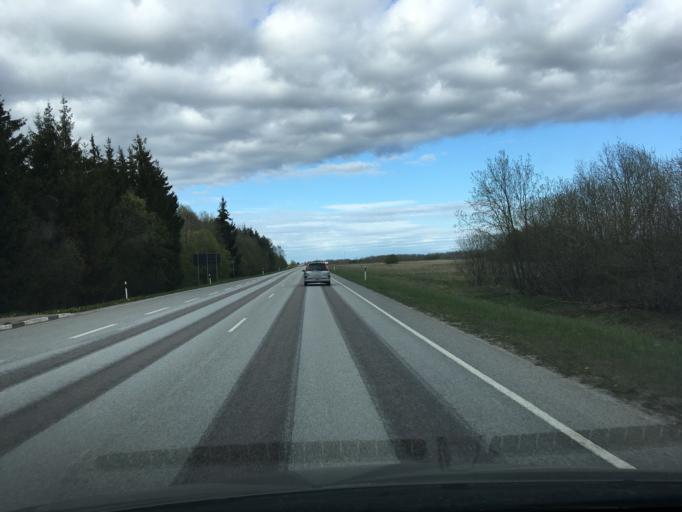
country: EE
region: Laeaene
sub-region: Lihula vald
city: Lihula
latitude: 58.6781
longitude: 23.7890
